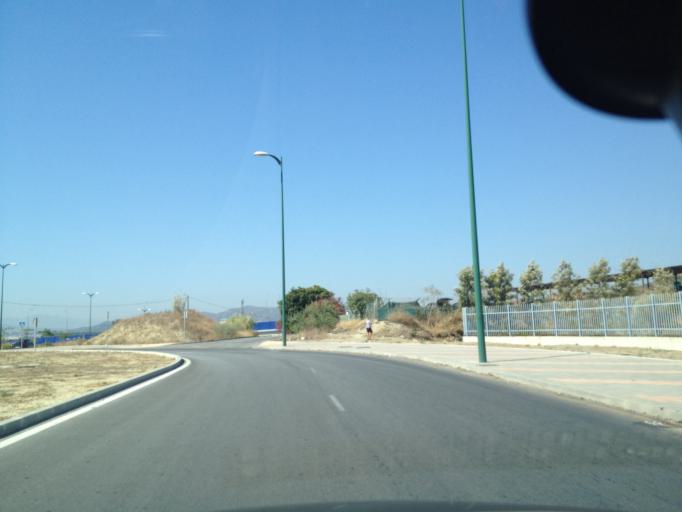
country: ES
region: Andalusia
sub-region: Provincia de Malaga
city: Alhaurin de la Torre
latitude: 36.7196
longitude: -4.5062
